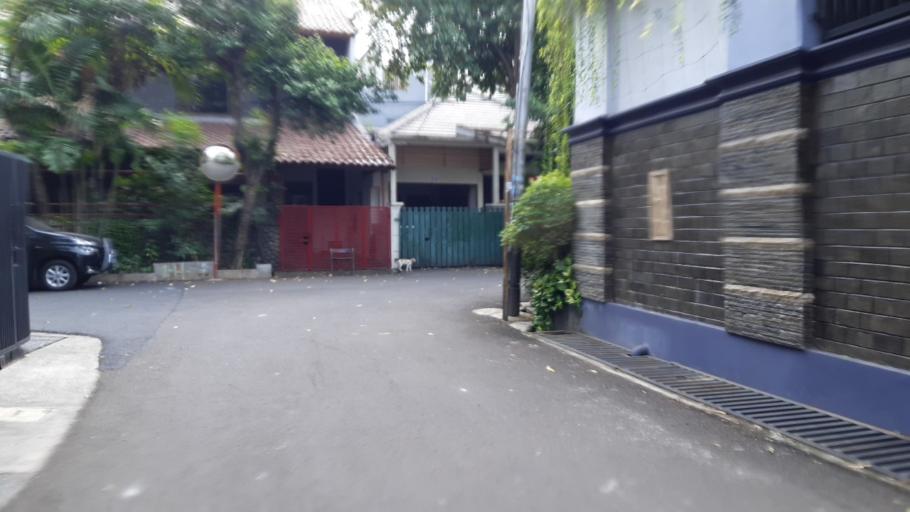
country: ID
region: Jakarta Raya
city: Jakarta
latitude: -6.2326
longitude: 106.8543
